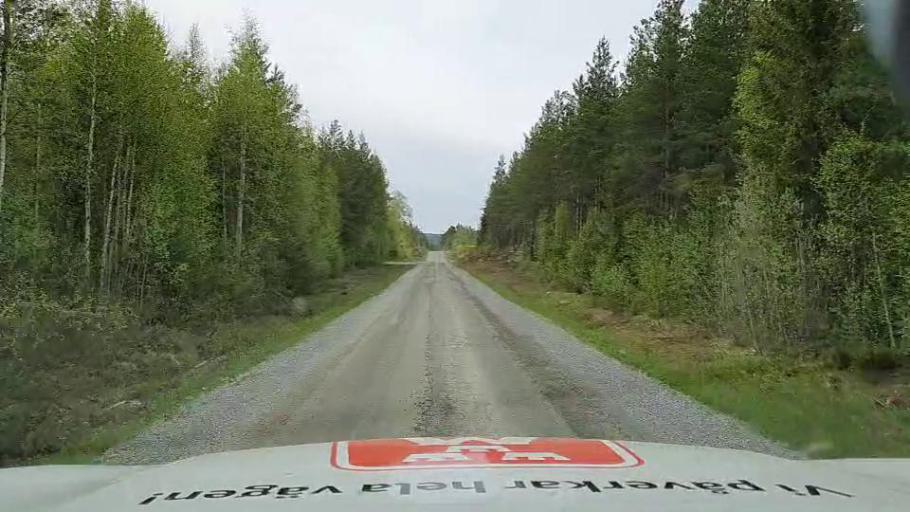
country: SE
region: Jaemtland
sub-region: Braecke Kommun
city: Braecke
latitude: 62.4718
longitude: 14.9160
